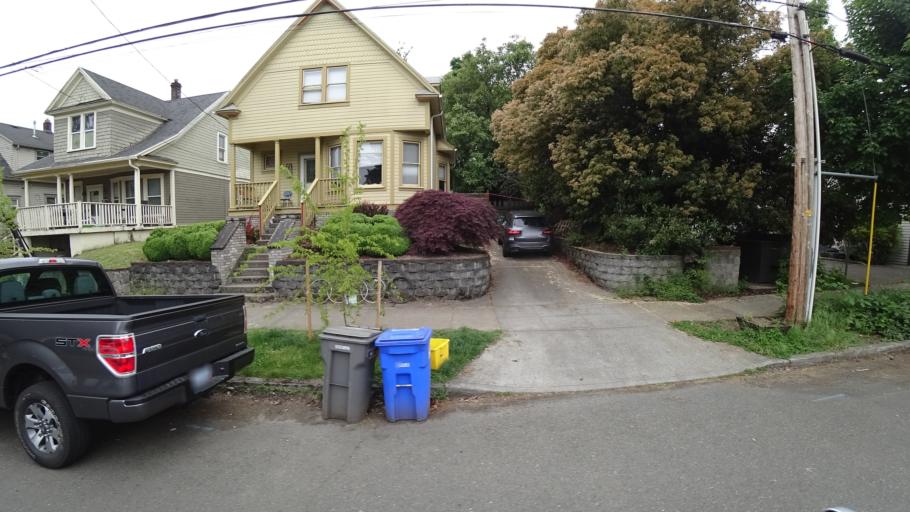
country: US
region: Oregon
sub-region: Multnomah County
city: Portland
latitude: 45.5468
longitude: -122.6627
